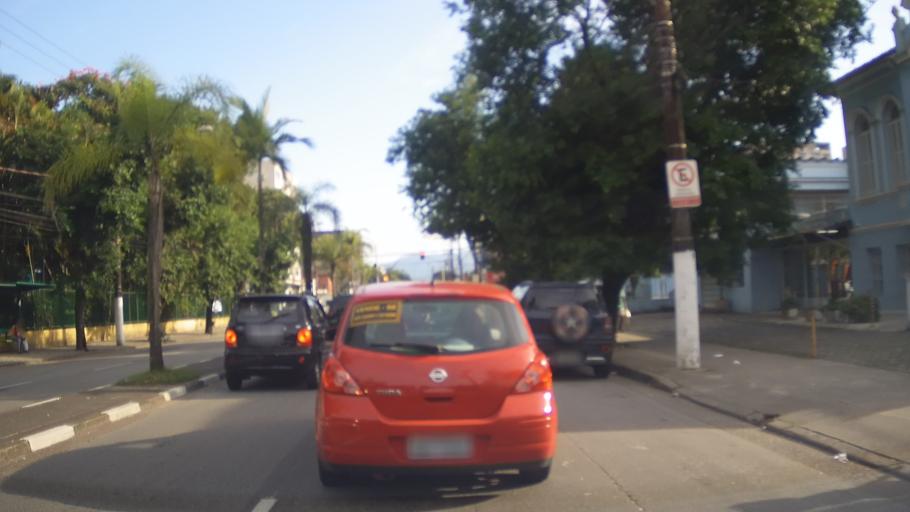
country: BR
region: Sao Paulo
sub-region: Santos
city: Santos
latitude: -23.9510
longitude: -46.3222
